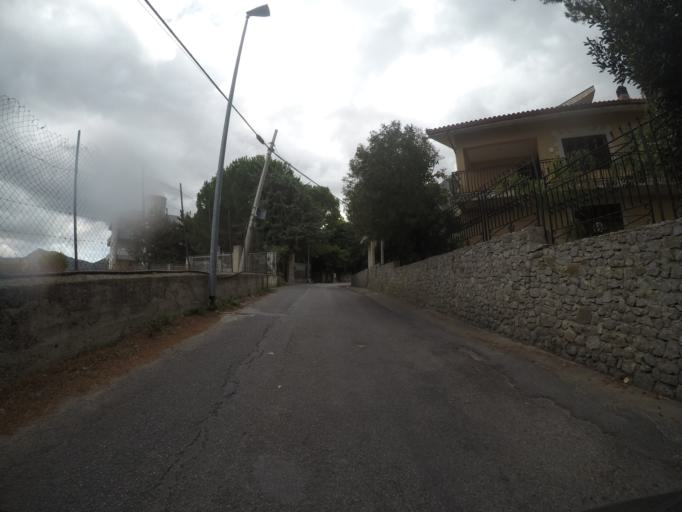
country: IT
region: Sicily
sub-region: Palermo
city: Carini
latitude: 38.1254
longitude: 13.1826
